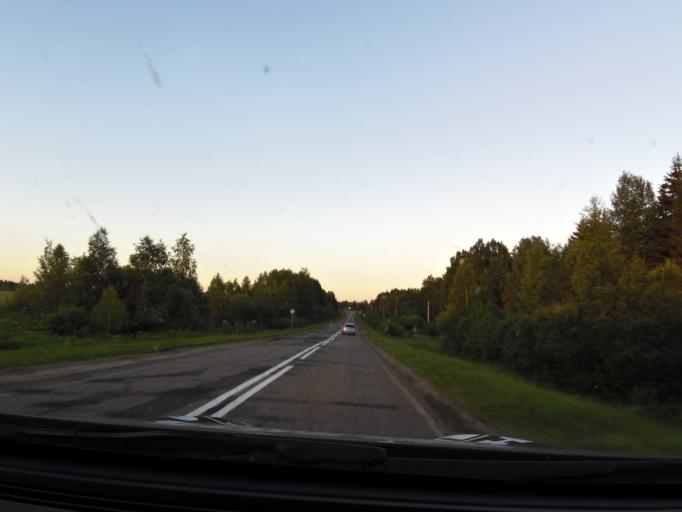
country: RU
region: Jaroslavl
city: Lyubim
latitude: 58.3499
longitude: 40.8068
